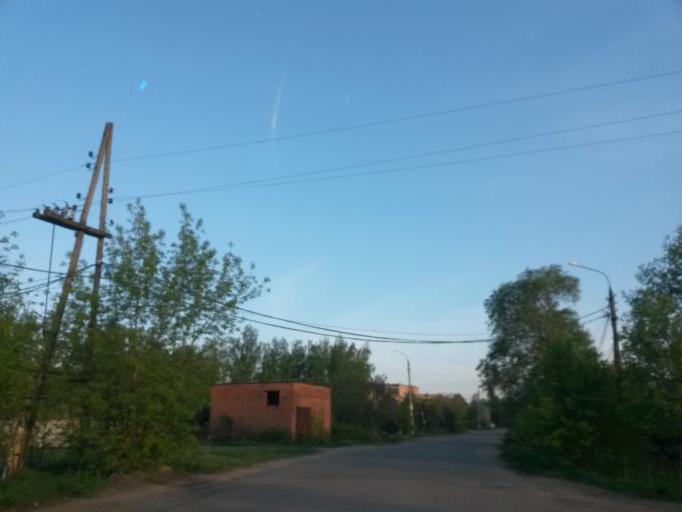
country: RU
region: Moskovskaya
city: Lyubuchany
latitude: 55.2375
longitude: 37.5435
